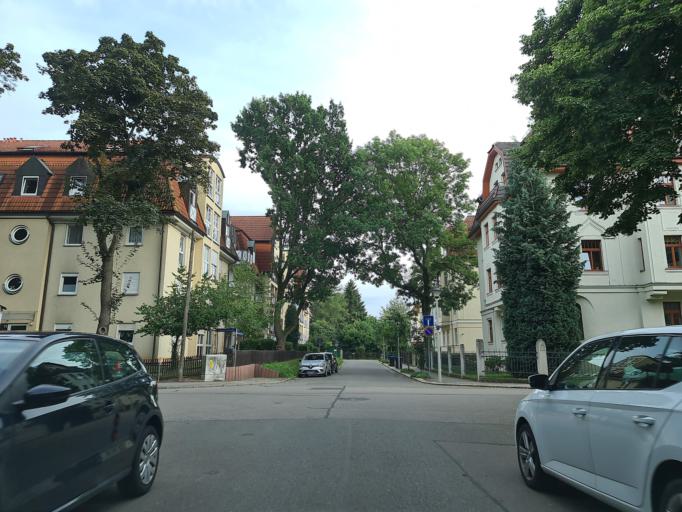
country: DE
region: Saxony
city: Zwickau
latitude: 50.7132
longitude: 12.4853
